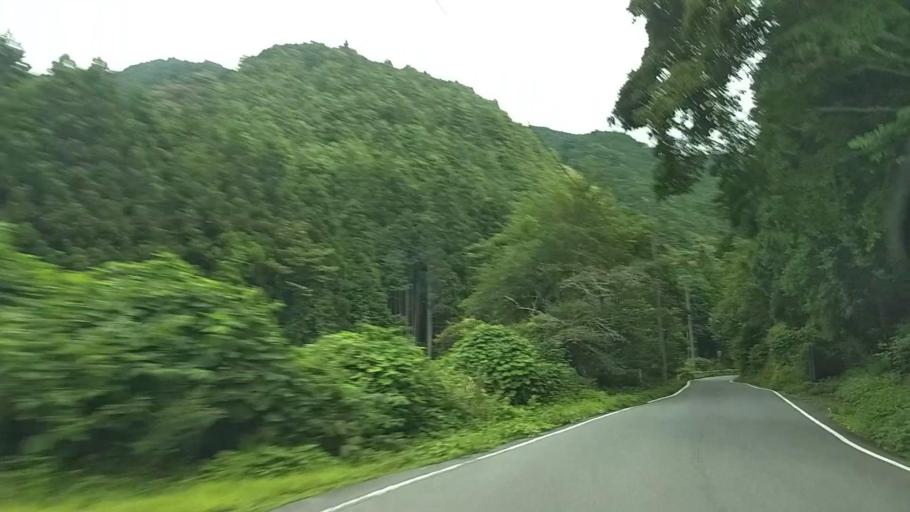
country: JP
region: Shizuoka
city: Fujinomiya
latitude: 35.1604
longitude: 138.5408
